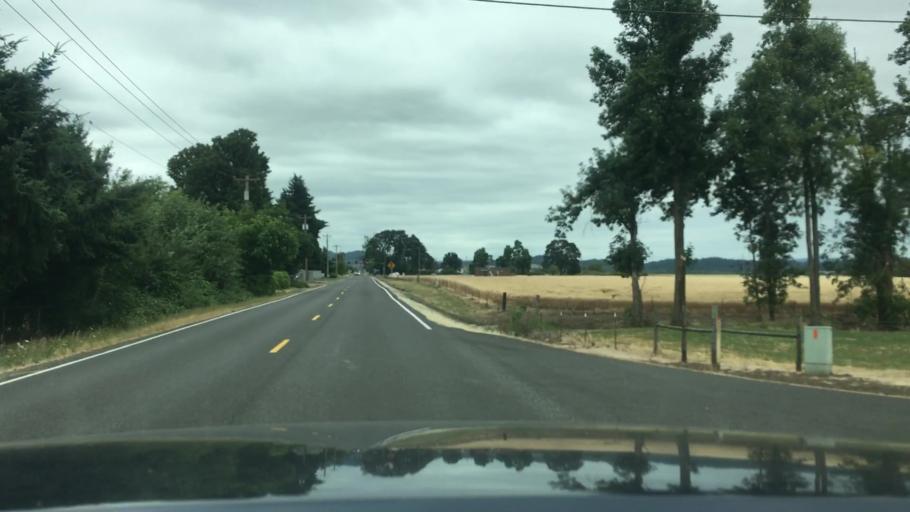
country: US
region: Oregon
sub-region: Lane County
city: Junction City
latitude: 44.1064
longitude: -123.2084
